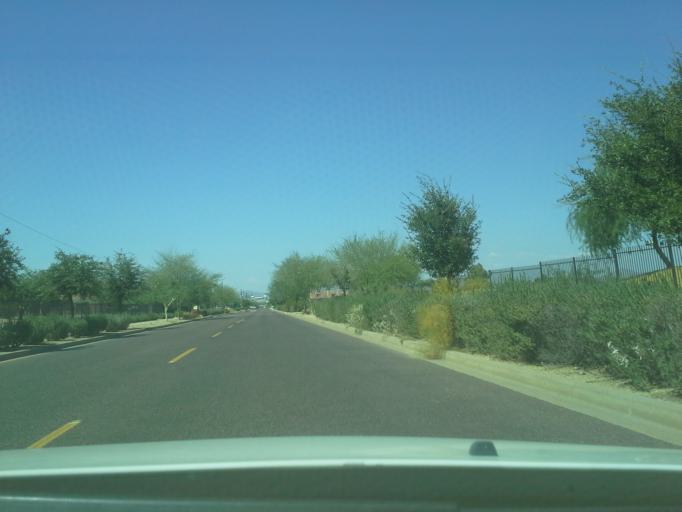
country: US
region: Arizona
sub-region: Maricopa County
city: Phoenix
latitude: 33.3592
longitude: -112.0660
